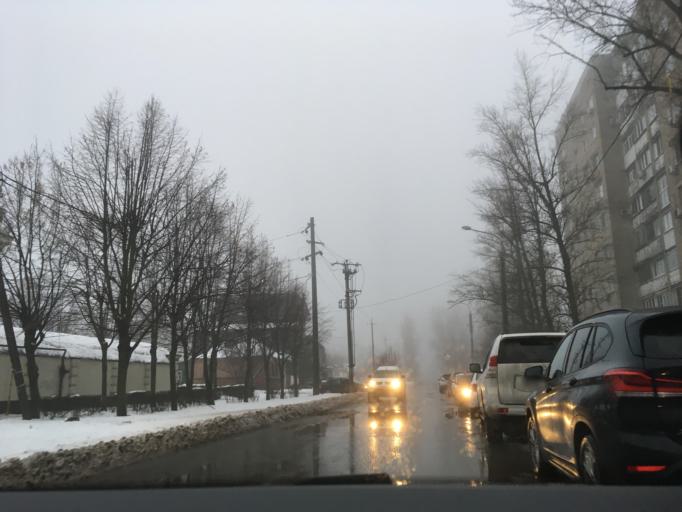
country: RU
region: Rostov
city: Rostov-na-Donu
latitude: 47.2091
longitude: 39.6708
